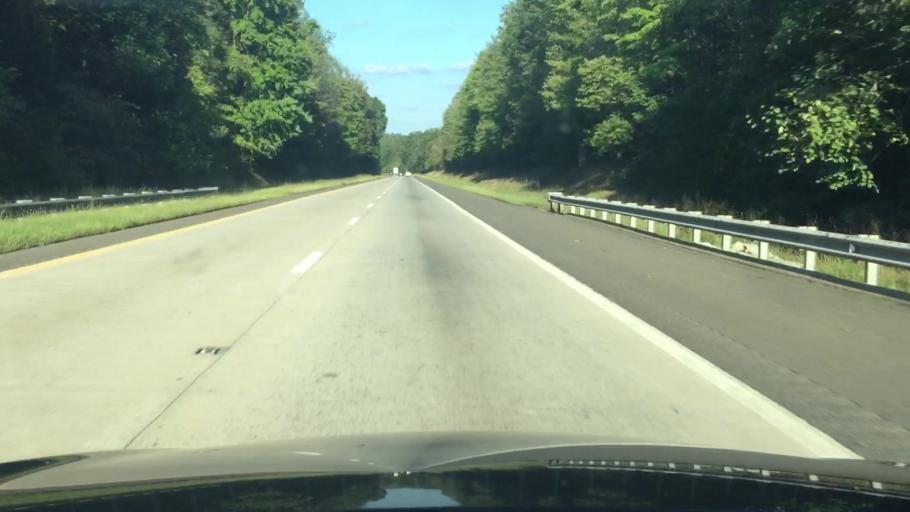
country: US
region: North Carolina
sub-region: Davie County
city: Mocksville
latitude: 35.8893
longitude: -80.6616
